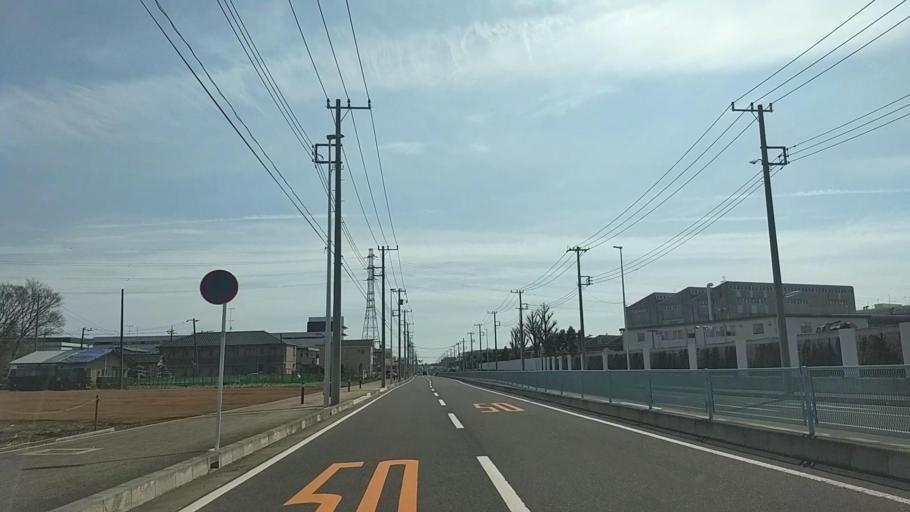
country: JP
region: Kanagawa
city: Fujisawa
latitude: 35.4024
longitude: 139.4553
